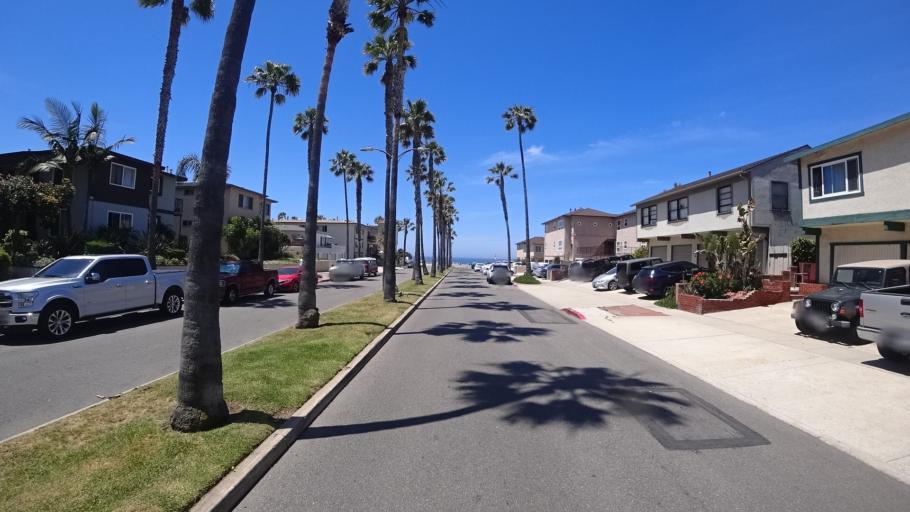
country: US
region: California
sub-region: Los Angeles County
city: Palos Verdes Estates
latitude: 33.8166
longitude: -118.3891
